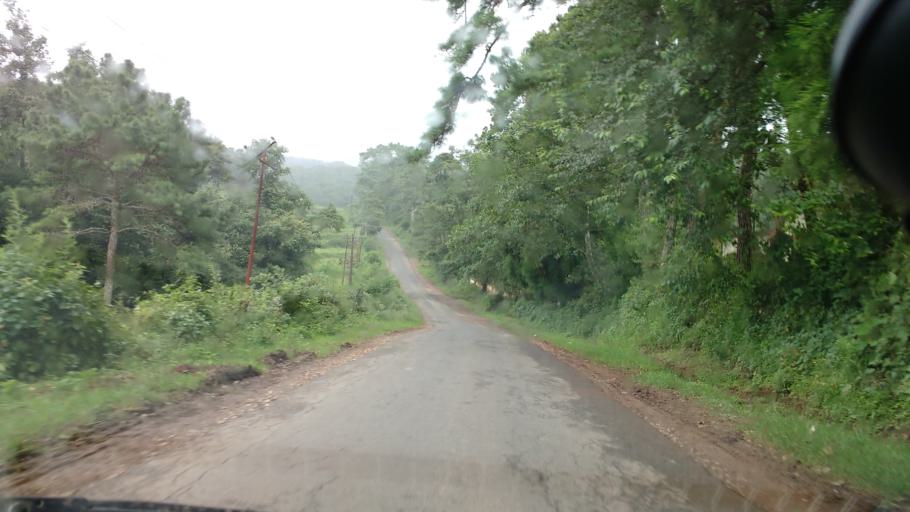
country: IN
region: Meghalaya
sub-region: East Khasi Hills
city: Shillong
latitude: 25.5451
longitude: 91.8461
